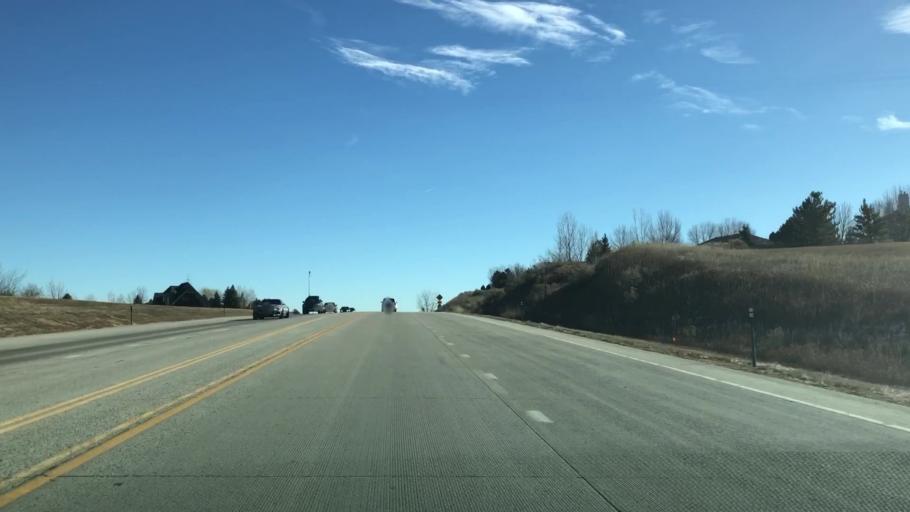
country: US
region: Colorado
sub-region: Weld County
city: Windsor
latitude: 40.4792
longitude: -104.9684
